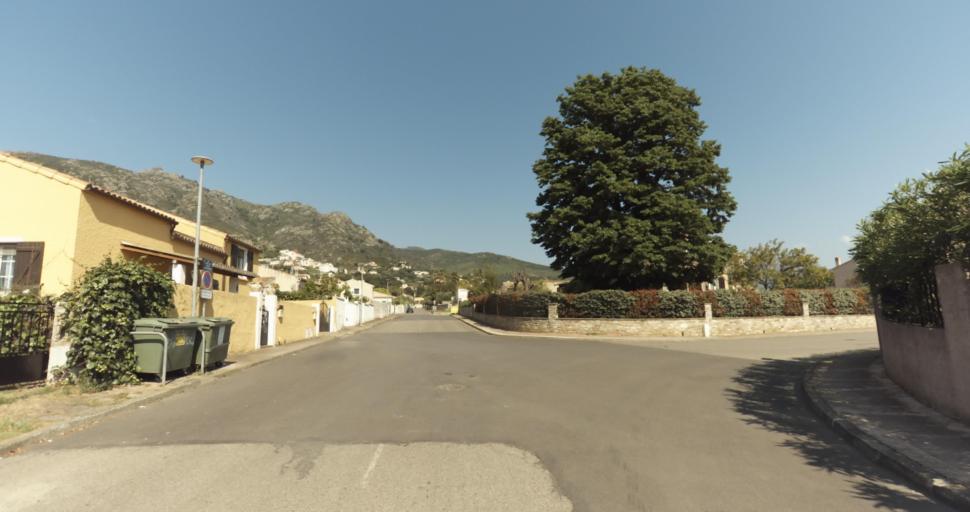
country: FR
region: Corsica
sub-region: Departement de la Haute-Corse
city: Biguglia
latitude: 42.6248
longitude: 9.4289
